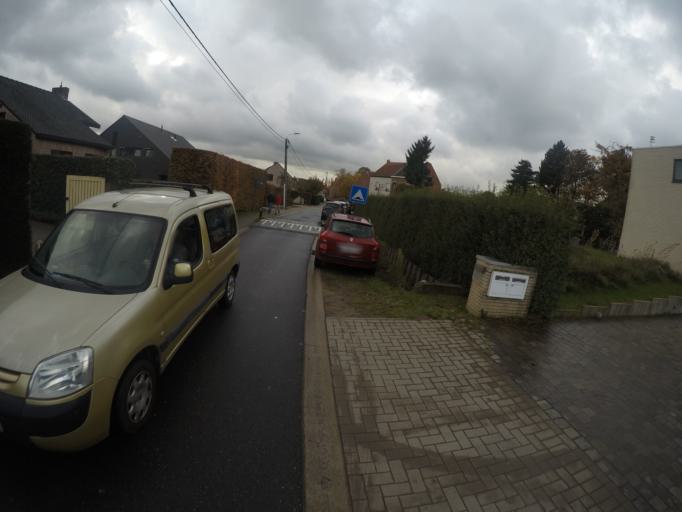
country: BE
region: Flanders
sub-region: Provincie Oost-Vlaanderen
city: Hamme
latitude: 51.1153
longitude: 4.1268
